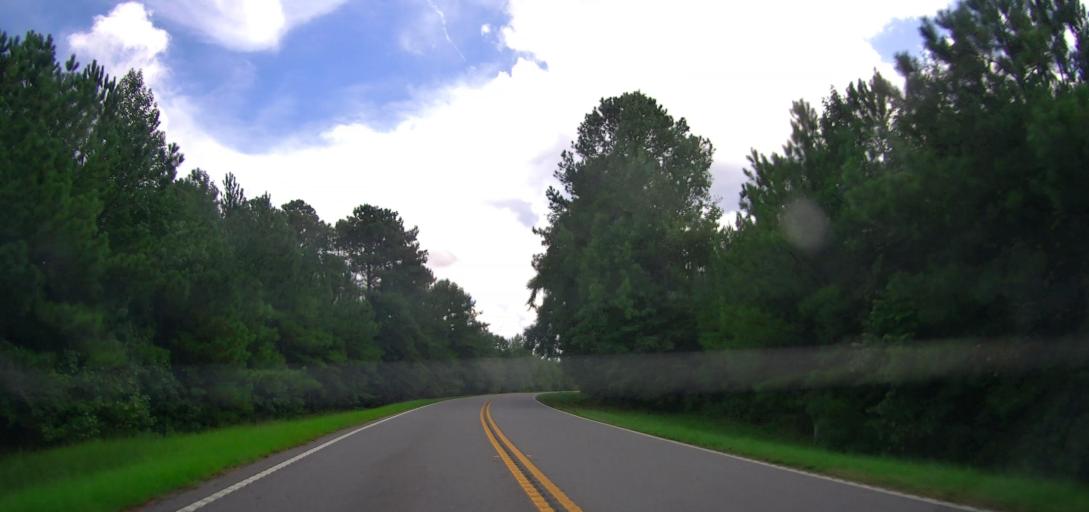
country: US
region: Georgia
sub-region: Talbot County
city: Talbotton
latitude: 32.6405
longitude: -84.4955
